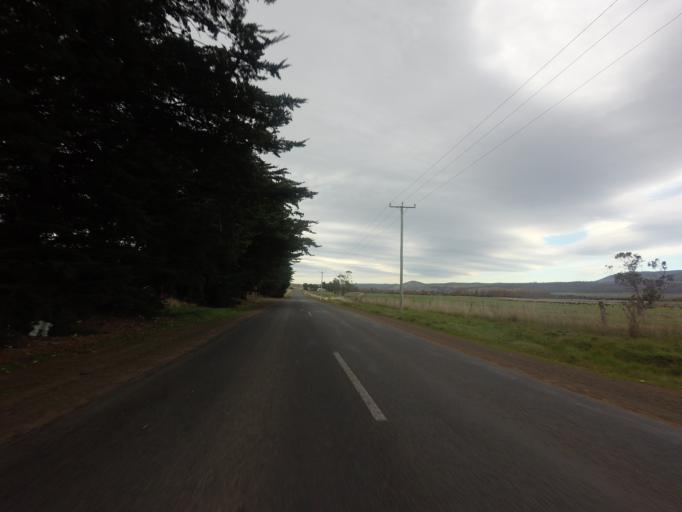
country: AU
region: Tasmania
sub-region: Derwent Valley
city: New Norfolk
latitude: -42.4990
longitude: 146.7321
